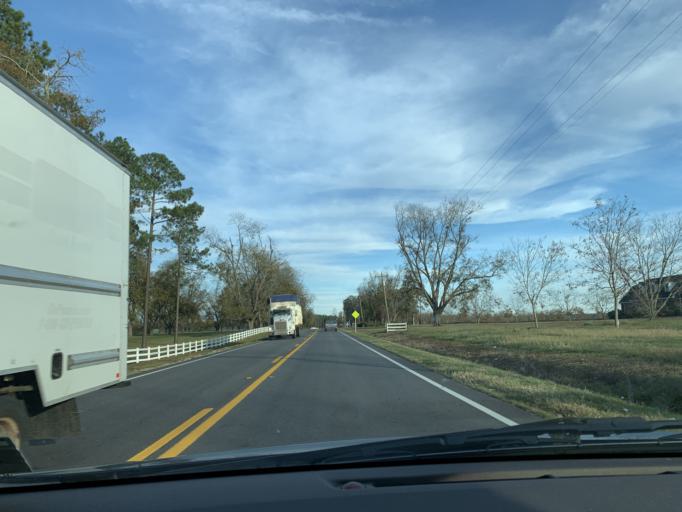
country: US
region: Georgia
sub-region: Irwin County
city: Ocilla
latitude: 31.5927
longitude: -83.2149
